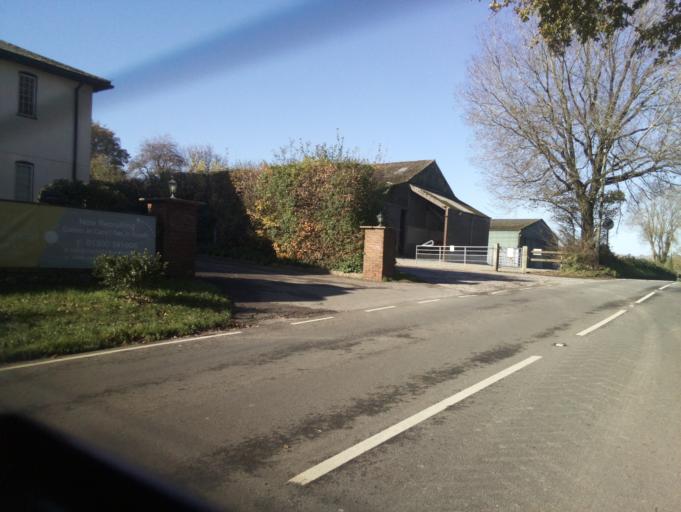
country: GB
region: England
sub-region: Dorset
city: Dorchester
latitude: 50.8141
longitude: -2.4815
